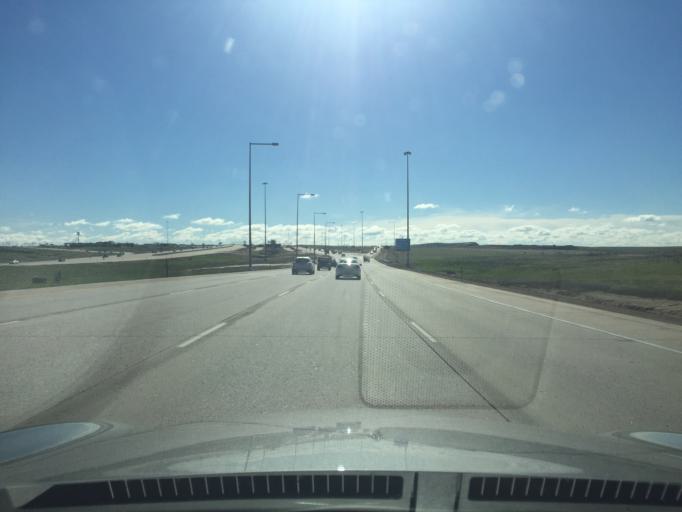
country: US
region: Colorado
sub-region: Adams County
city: Aurora
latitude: 39.8338
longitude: -104.7323
